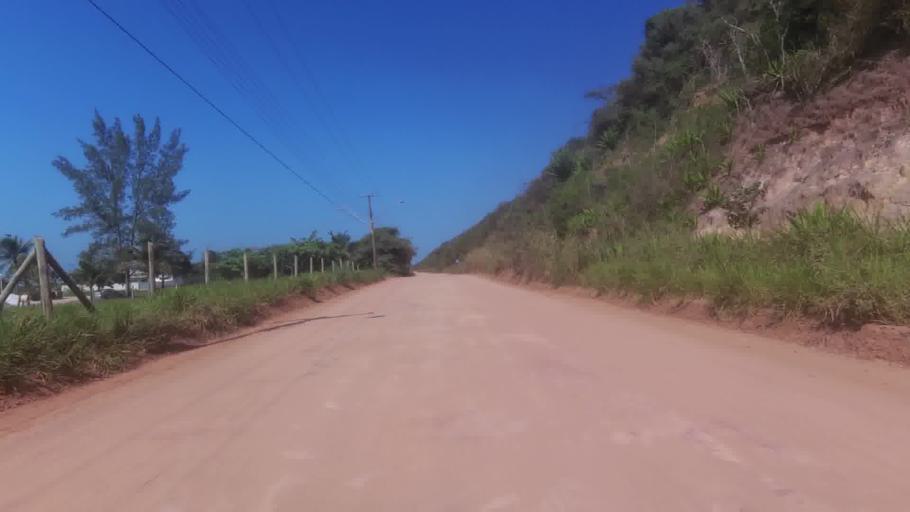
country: BR
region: Espirito Santo
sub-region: Marataizes
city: Marataizes
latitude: -21.0762
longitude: -40.8408
